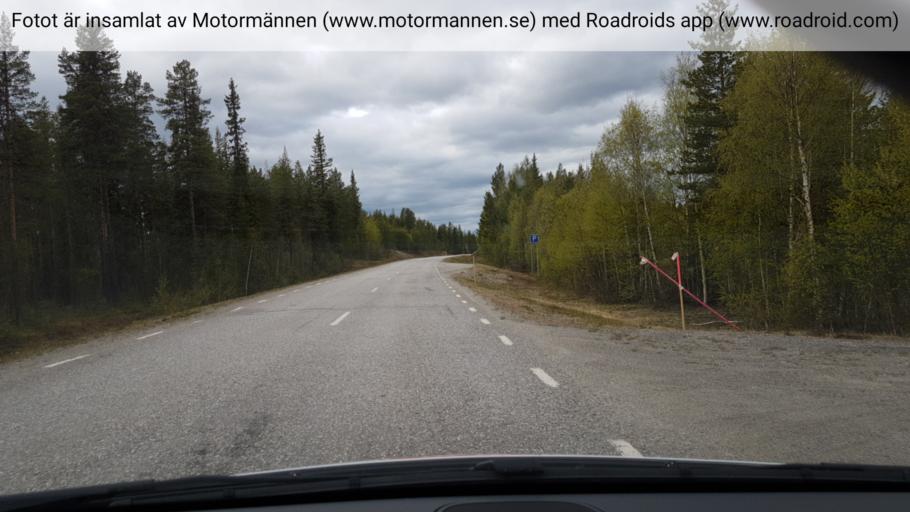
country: SE
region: Vaesterbotten
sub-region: Lycksele Kommun
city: Soderfors
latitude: 65.2652
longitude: 18.0214
